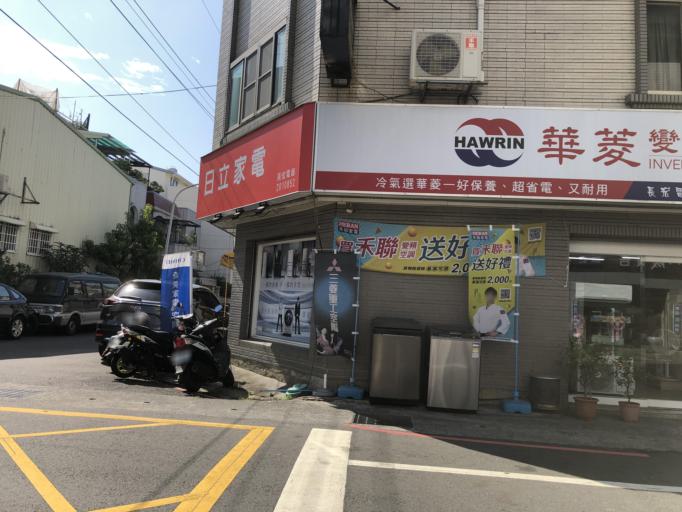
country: TW
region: Taiwan
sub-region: Tainan
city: Tainan
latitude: 23.0187
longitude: 120.2415
